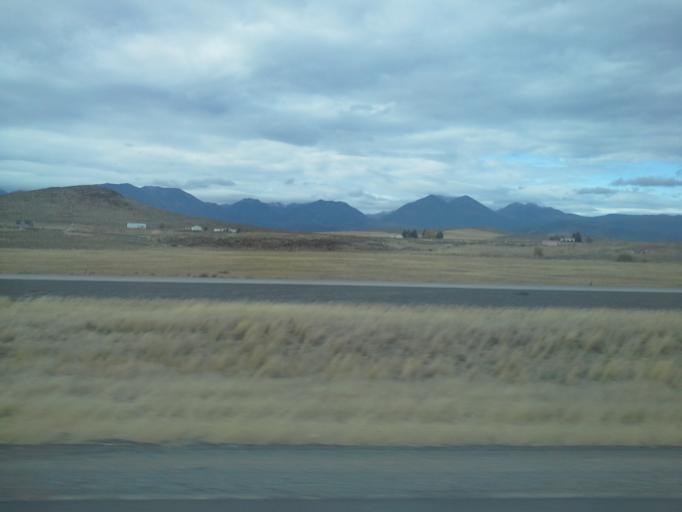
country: US
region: Oregon
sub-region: Union County
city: Union
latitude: 44.9888
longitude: -117.8963
